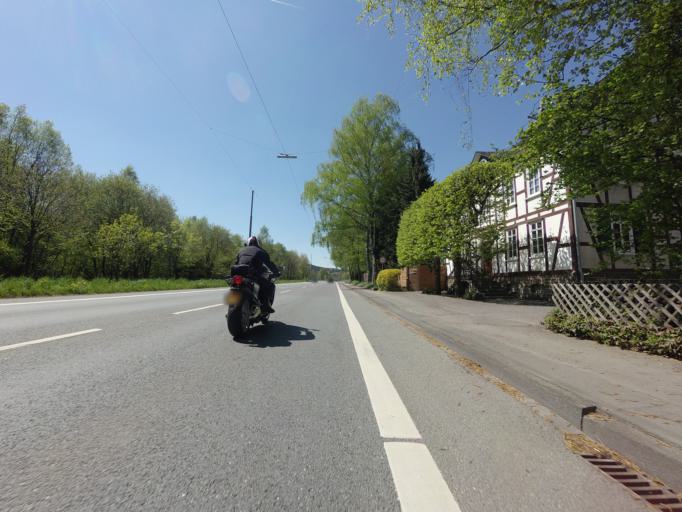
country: DE
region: North Rhine-Westphalia
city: Kreuztal
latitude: 50.9630
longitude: 8.0342
